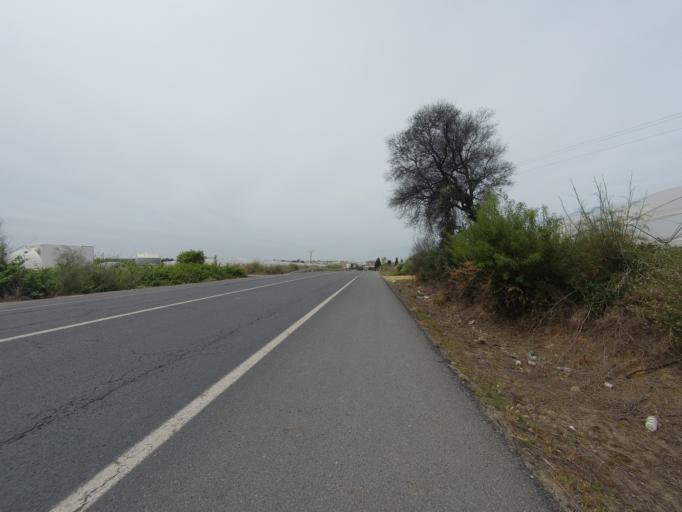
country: ES
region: Andalusia
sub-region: Provincia de Huelva
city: Palos de la Frontera
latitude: 37.2377
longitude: -6.8847
